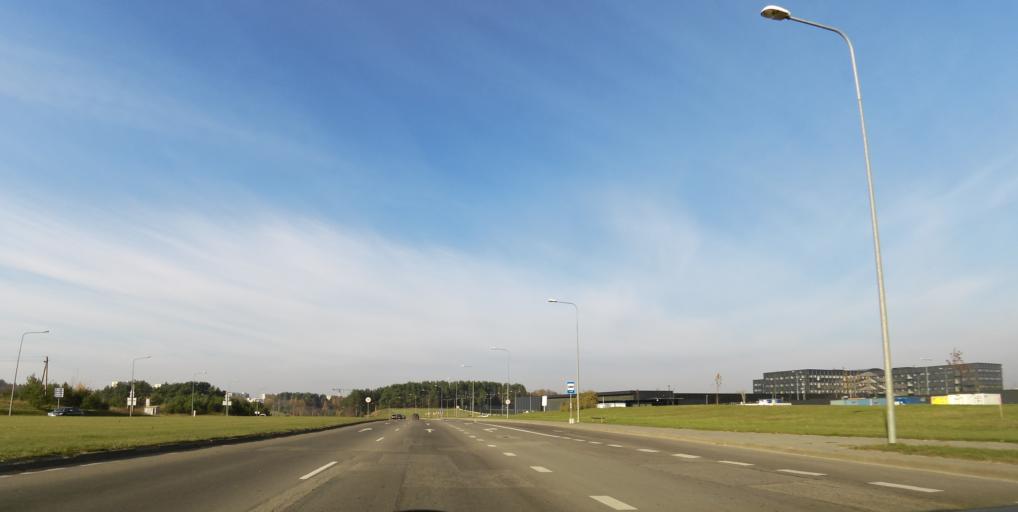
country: LT
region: Vilnius County
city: Pilaite
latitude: 54.7040
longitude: 25.2014
